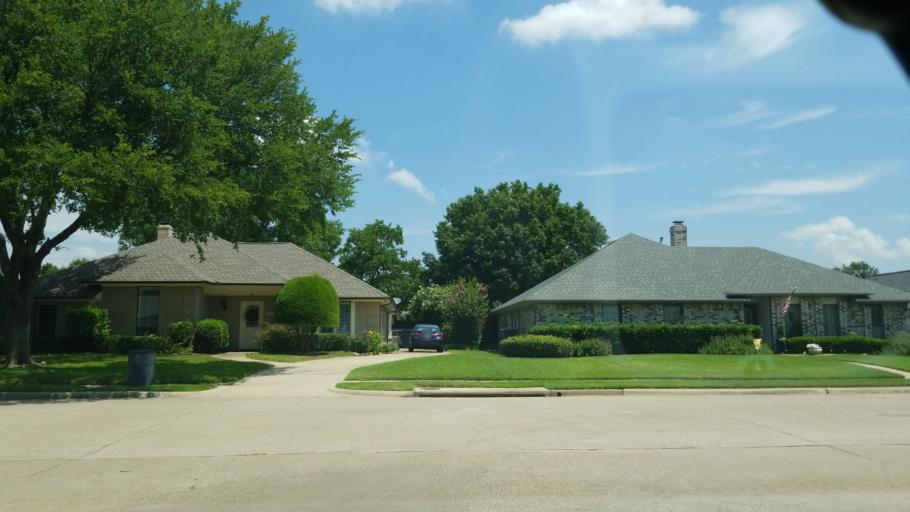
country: US
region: Texas
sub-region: Dallas County
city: Coppell
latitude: 32.9687
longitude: -96.9683
